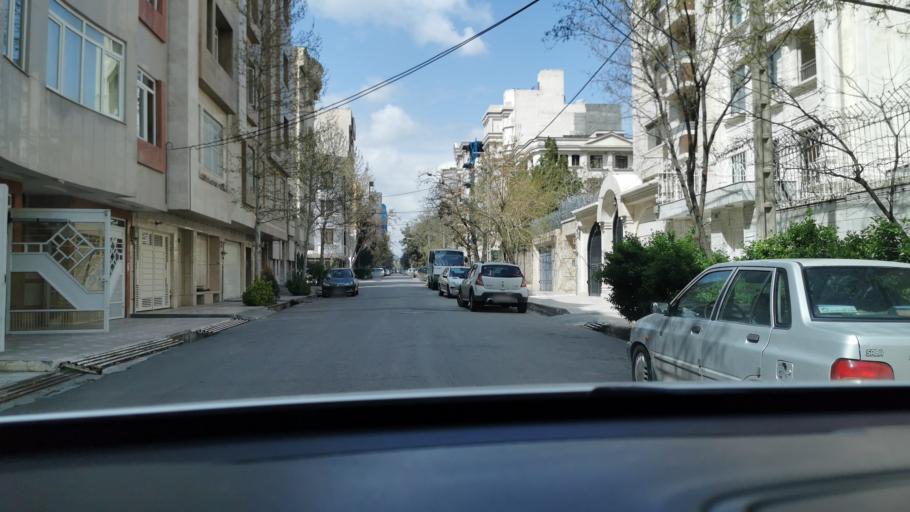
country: IR
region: Razavi Khorasan
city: Mashhad
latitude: 36.3220
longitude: 59.5301
